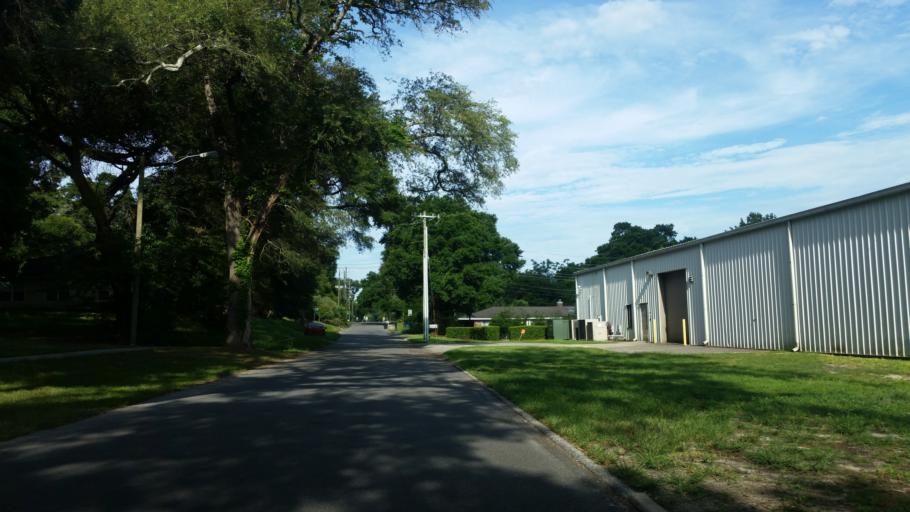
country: US
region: Florida
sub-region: Escambia County
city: Pensacola
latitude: 30.4159
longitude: -87.2470
